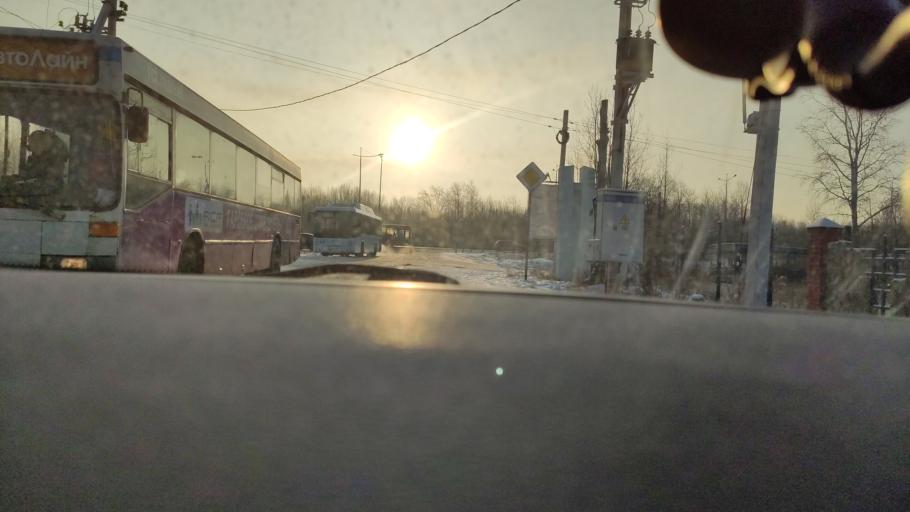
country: RU
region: Perm
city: Kondratovo
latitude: 57.9424
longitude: 56.0602
